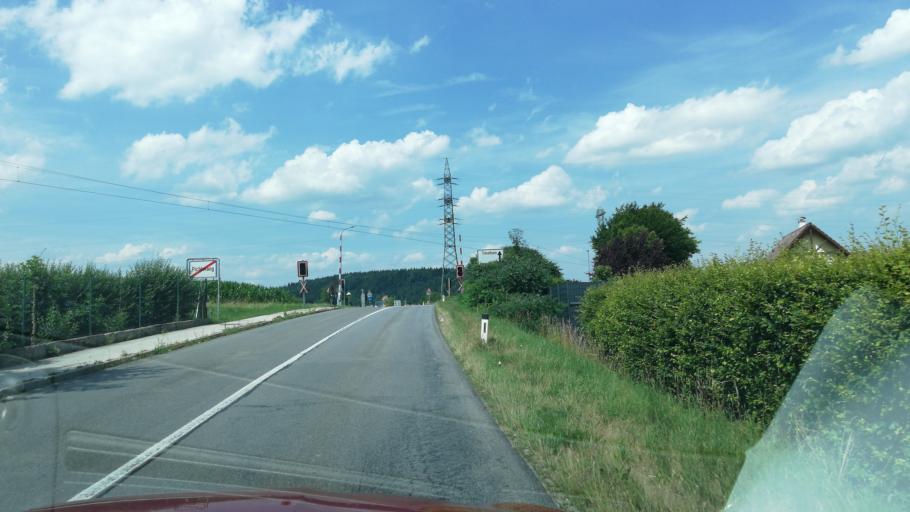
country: AT
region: Upper Austria
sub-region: Politischer Bezirk Vocklabruck
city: Timelkam
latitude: 47.9939
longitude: 13.6149
